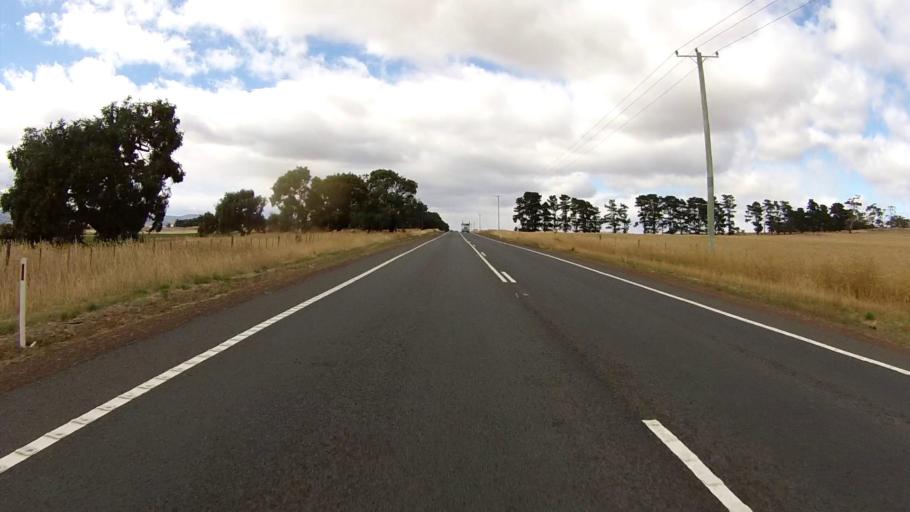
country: AU
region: Tasmania
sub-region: Northern Midlands
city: Evandale
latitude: -41.9085
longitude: 147.4804
